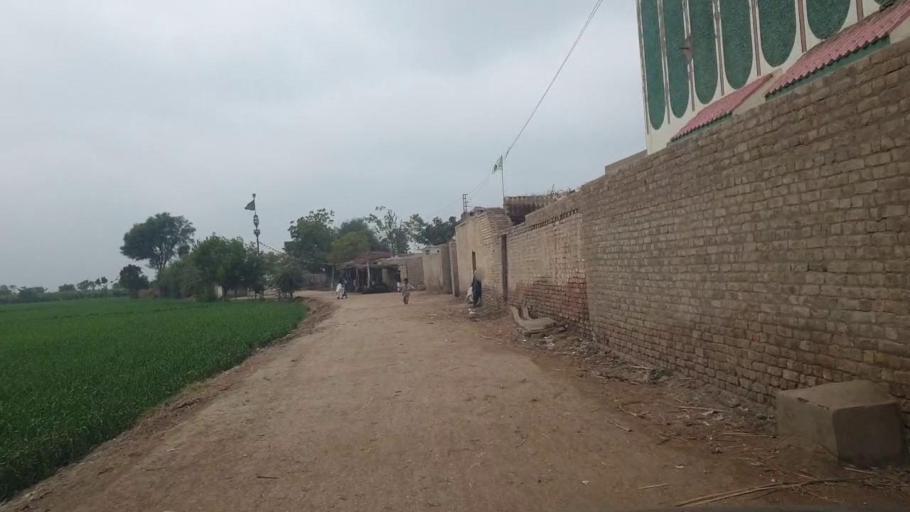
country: PK
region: Sindh
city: Shahdadpur
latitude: 25.8721
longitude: 68.6863
